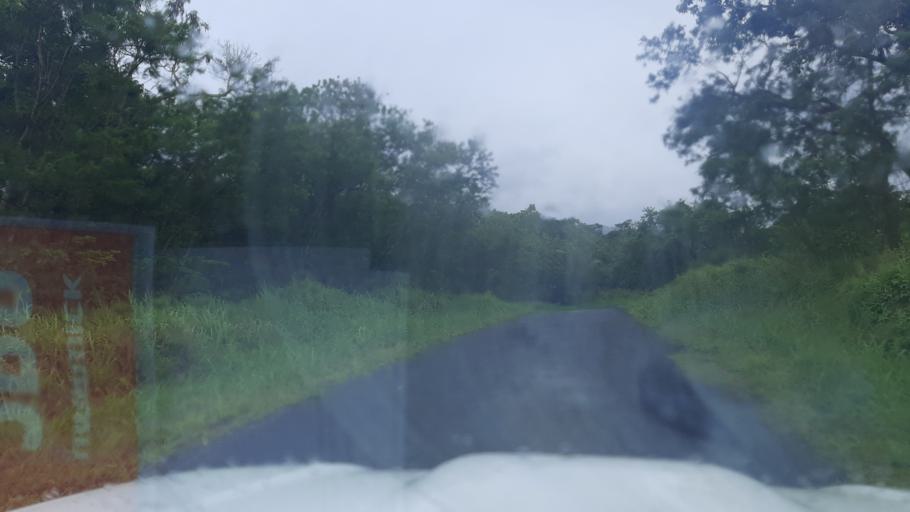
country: VU
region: Shefa
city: Port-Vila
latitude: -17.6393
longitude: 168.2116
